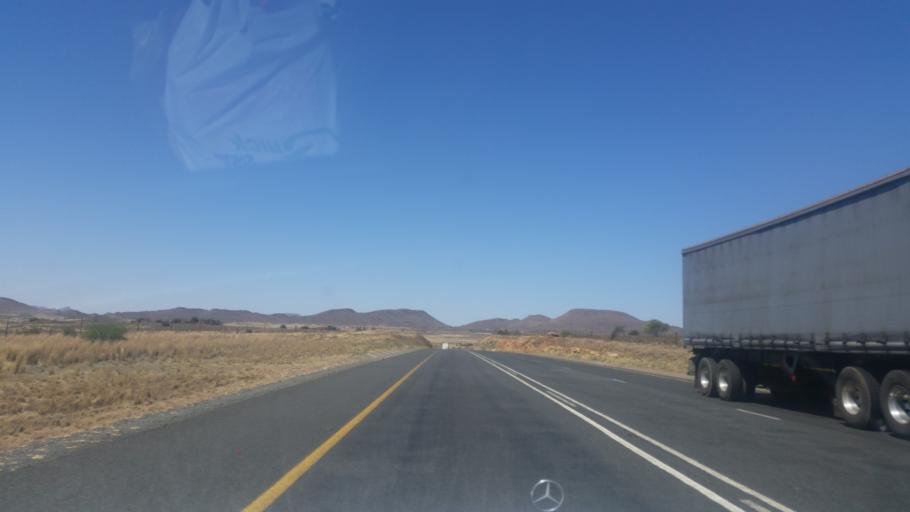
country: ZA
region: Northern Cape
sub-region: Pixley ka Seme District Municipality
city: Colesberg
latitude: -30.6203
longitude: 25.3396
